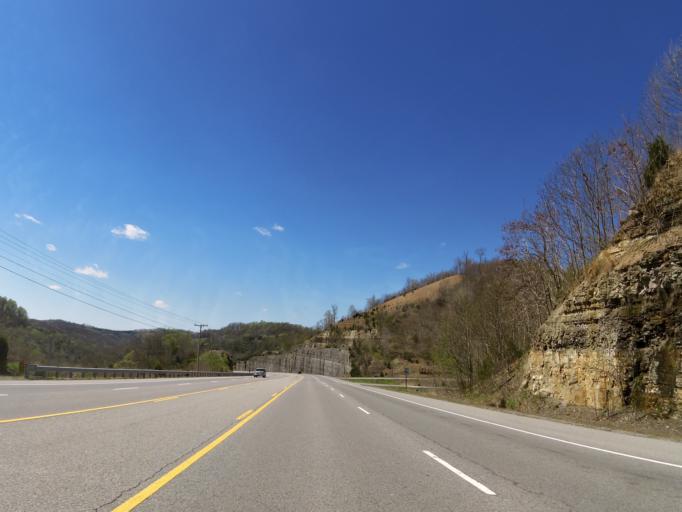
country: US
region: Tennessee
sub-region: DeKalb County
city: Smithville
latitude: 35.9996
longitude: -85.8951
